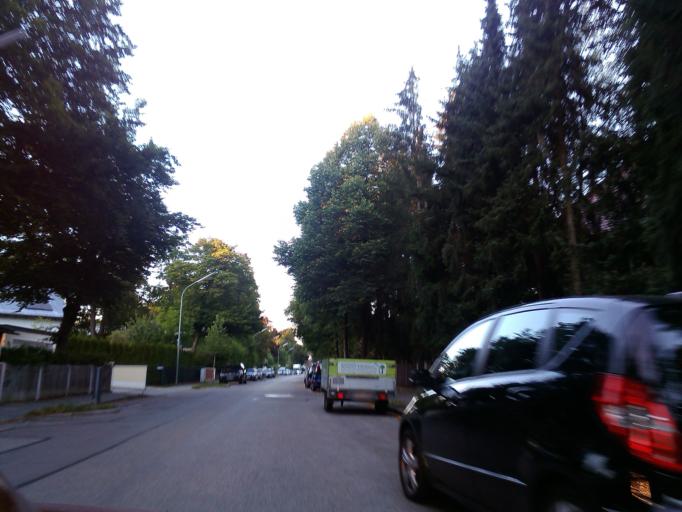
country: DE
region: Bavaria
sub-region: Upper Bavaria
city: Planegg
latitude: 48.1085
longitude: 11.4182
